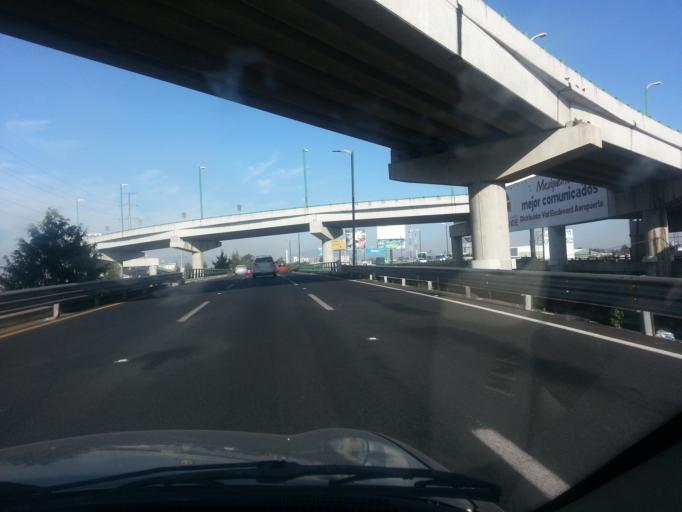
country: MX
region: Mexico
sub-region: San Mateo Atenco
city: Santa Maria la Asuncion
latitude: 19.2865
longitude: -99.5552
